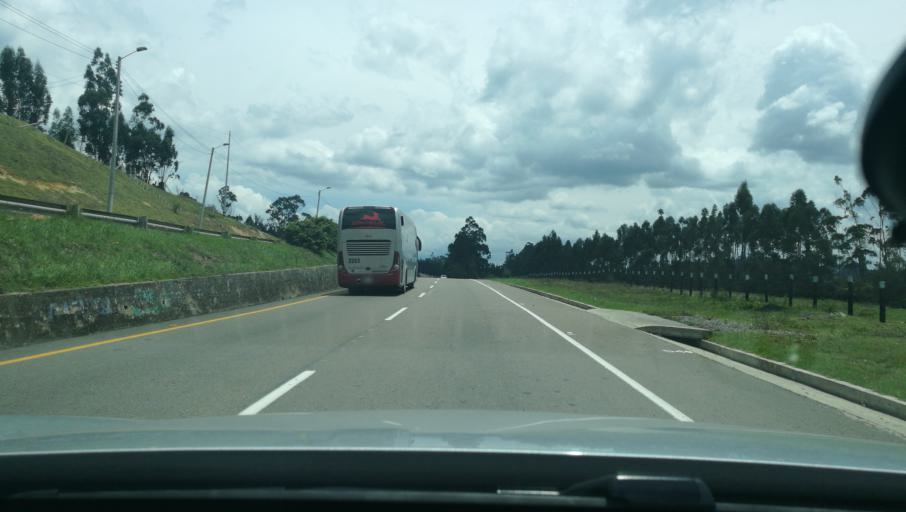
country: CO
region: Boyaca
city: Combita
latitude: 5.6592
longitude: -73.2760
